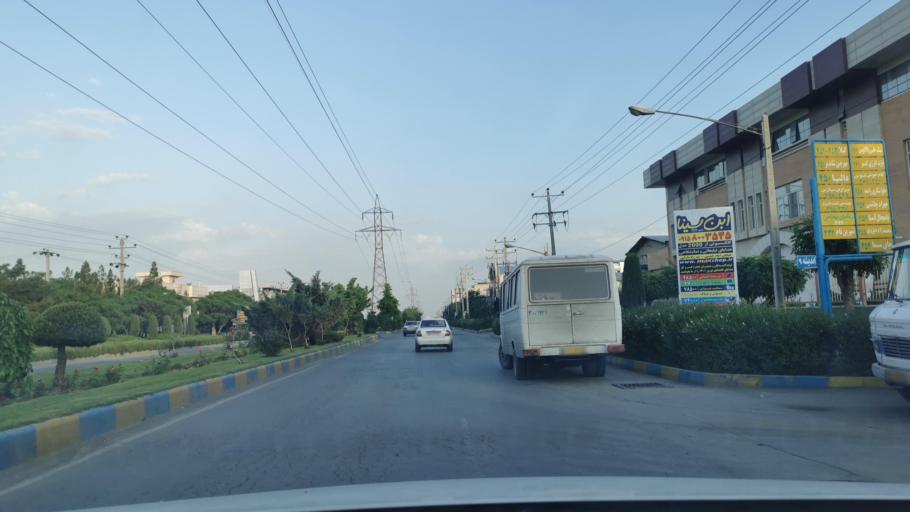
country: IR
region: Razavi Khorasan
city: Torqabeh
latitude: 36.4256
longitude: 59.4229
